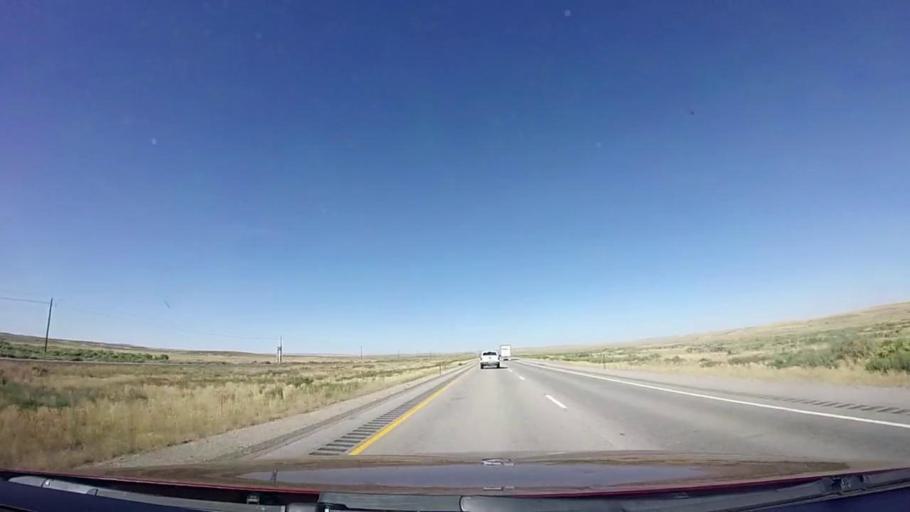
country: US
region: Wyoming
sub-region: Carbon County
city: Rawlins
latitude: 41.7825
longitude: -107.4249
